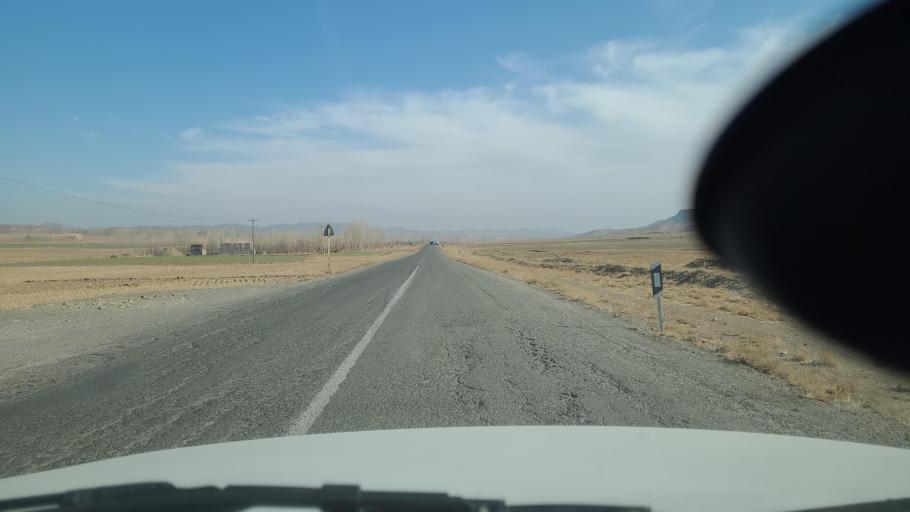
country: IR
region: Razavi Khorasan
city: Fariman
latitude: 35.5879
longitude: 59.6565
